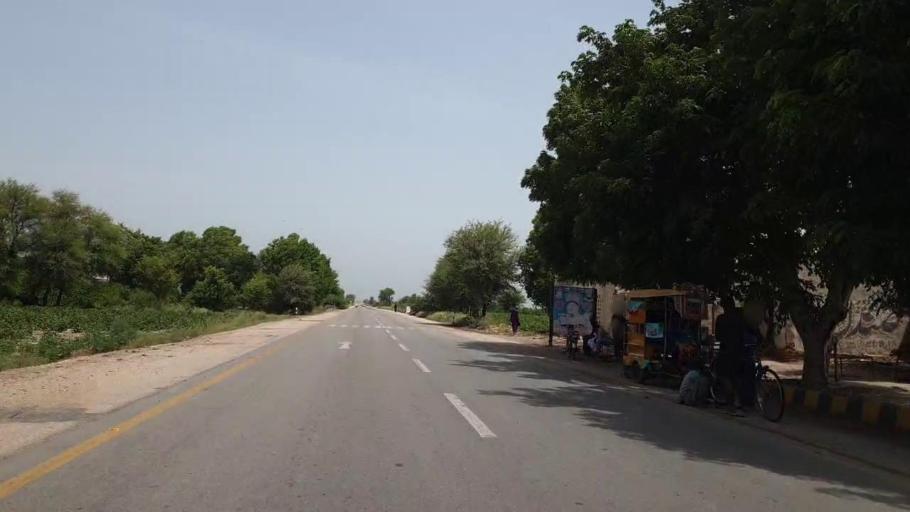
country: PK
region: Sindh
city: Shahpur Chakar
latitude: 26.1568
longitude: 68.6329
